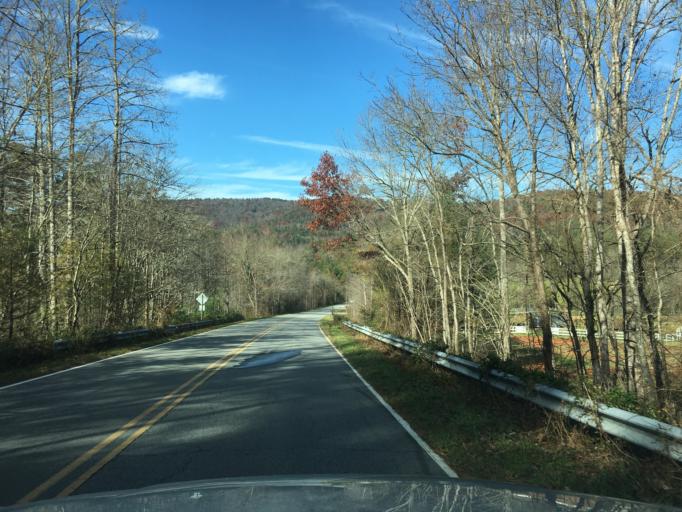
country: US
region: North Carolina
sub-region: Henderson County
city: Etowah
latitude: 35.2326
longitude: -82.5998
